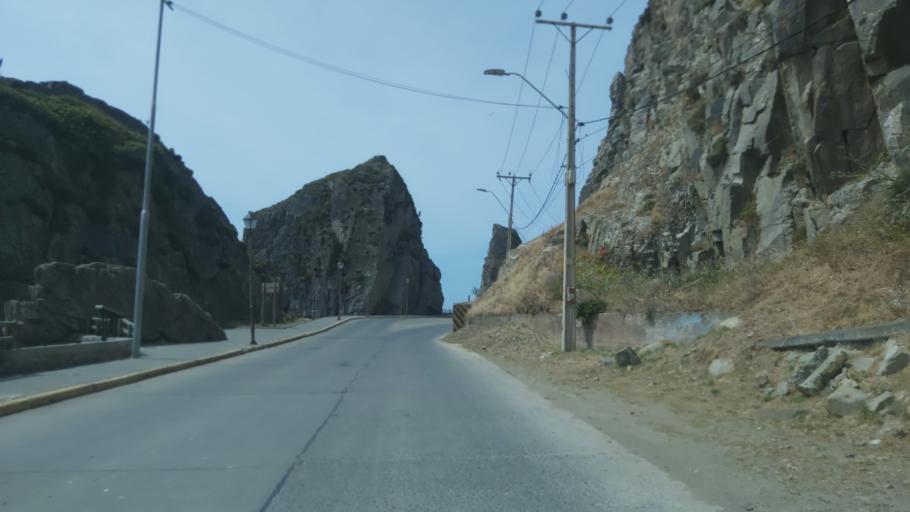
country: CL
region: Maule
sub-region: Provincia de Talca
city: Constitucion
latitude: -35.3273
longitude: -72.4294
